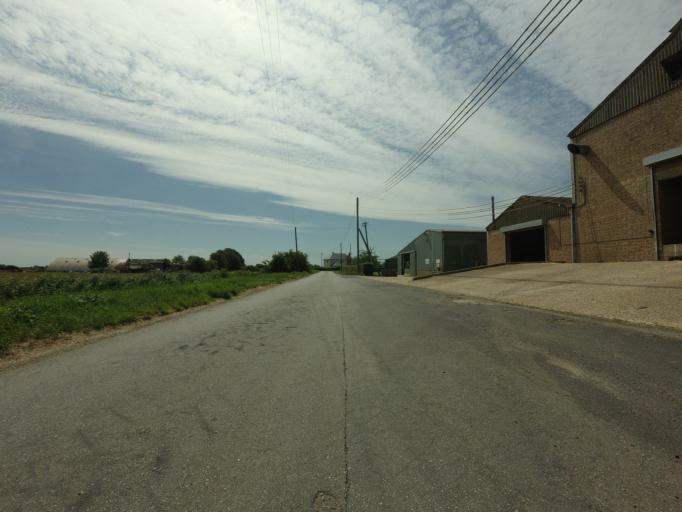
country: GB
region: England
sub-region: Kent
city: Stone
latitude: 51.0154
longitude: 0.7942
